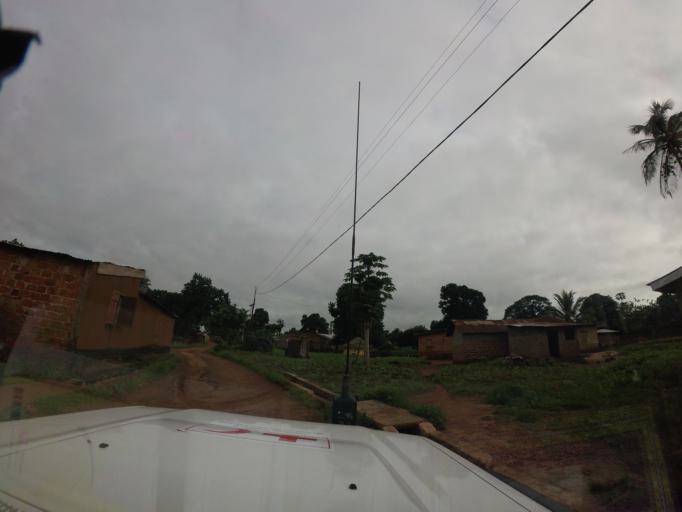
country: GN
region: Kindia
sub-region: Kindia
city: Kindia
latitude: 10.0118
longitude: -12.8995
